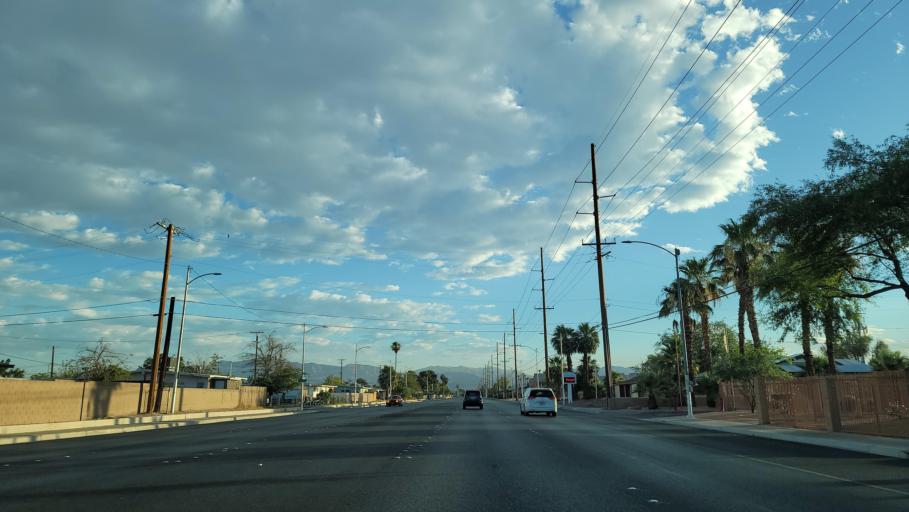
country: US
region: Nevada
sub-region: Clark County
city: North Las Vegas
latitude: 36.1895
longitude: -115.0983
